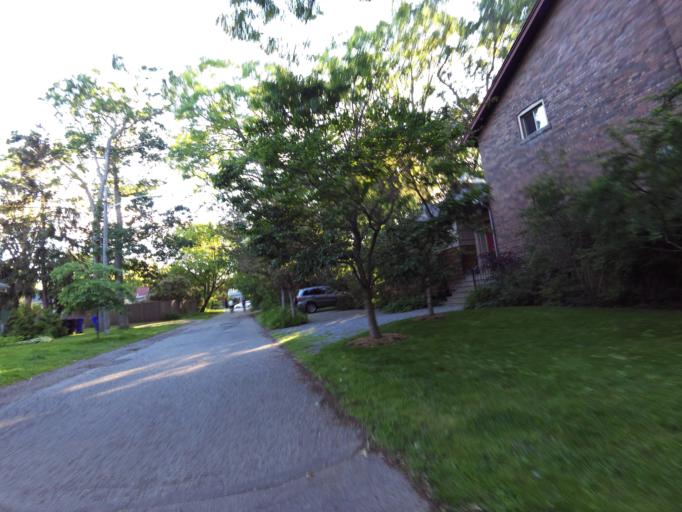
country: CA
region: Ontario
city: Scarborough
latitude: 43.6884
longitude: -79.2654
